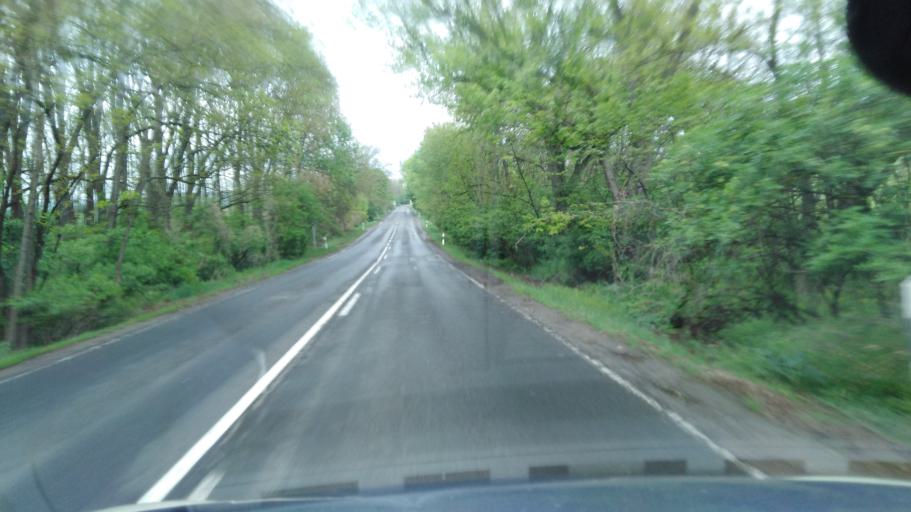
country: HU
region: Nograd
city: Szecseny
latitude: 48.0945
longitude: 19.5326
